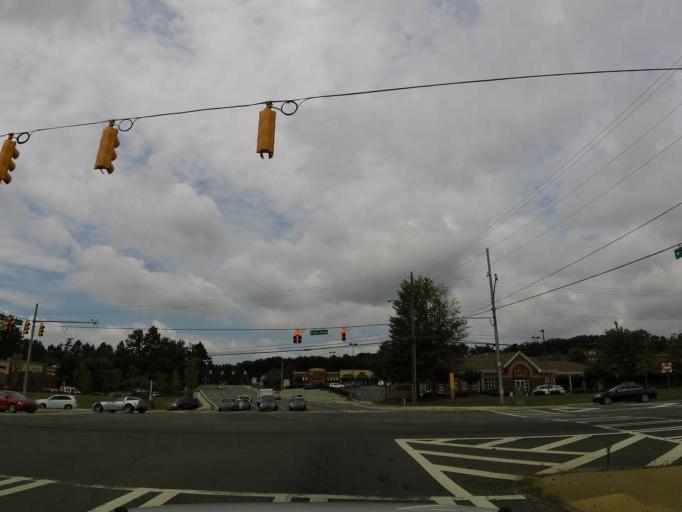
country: US
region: Georgia
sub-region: Cobb County
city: Kennesaw
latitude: 34.0218
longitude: -84.6253
